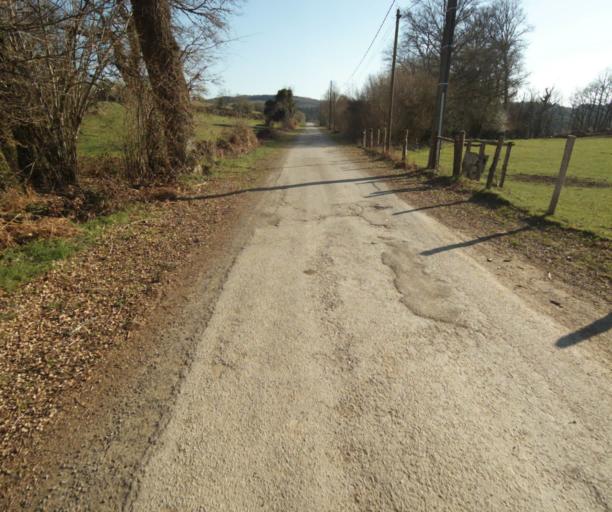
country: FR
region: Limousin
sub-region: Departement de la Correze
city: Chamboulive
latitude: 45.5009
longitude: 1.7256
